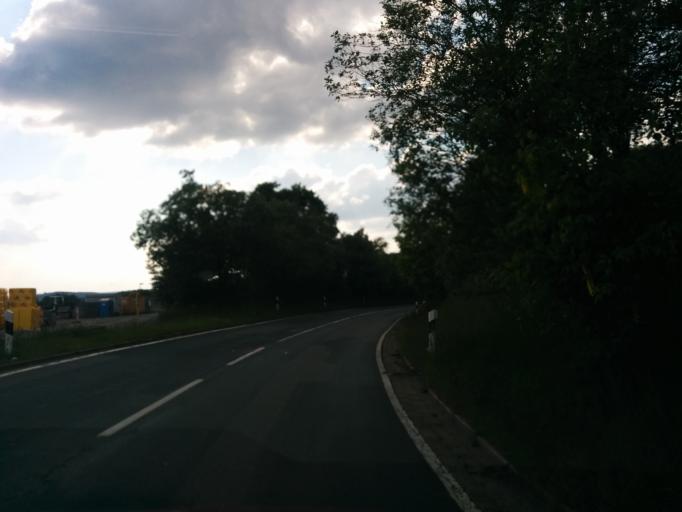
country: DE
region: Lower Saxony
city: Sankt Andreasberg
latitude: 51.7160
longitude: 10.5319
